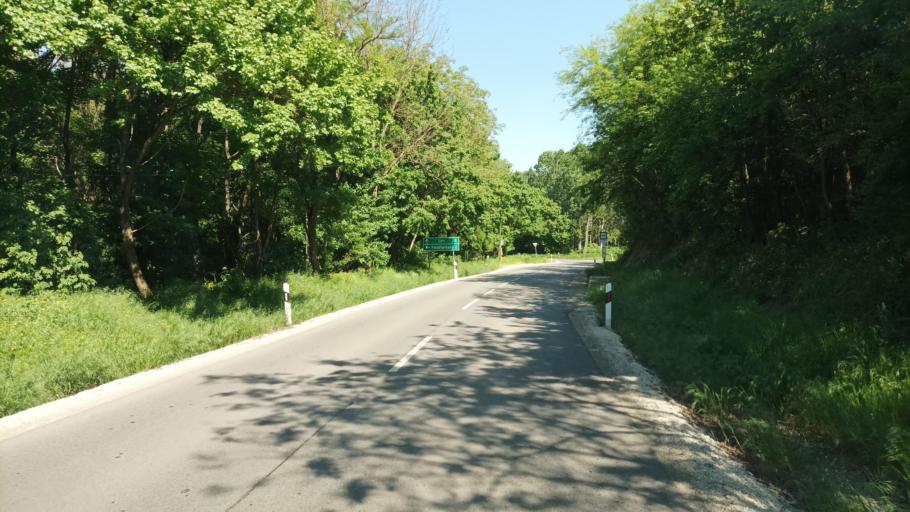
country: HU
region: Pest
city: Gomba
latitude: 47.3880
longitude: 19.5006
